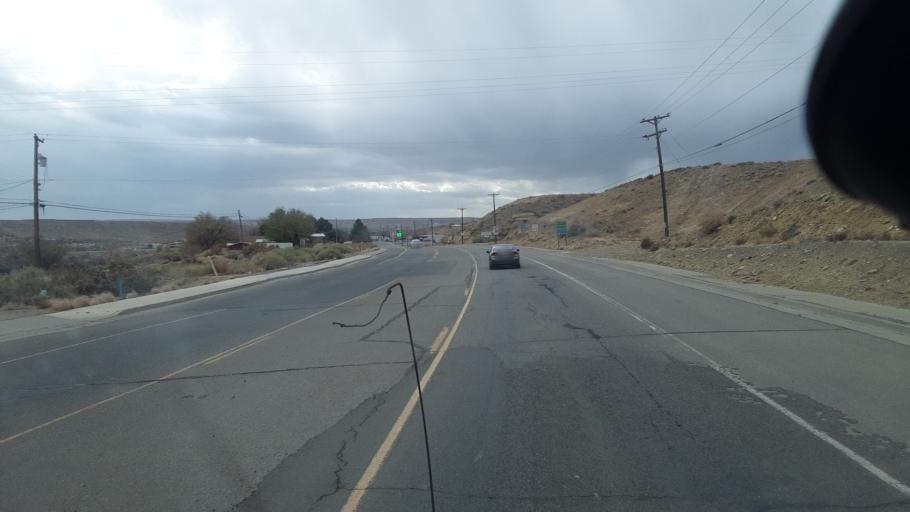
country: US
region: New Mexico
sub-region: San Juan County
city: Farmington
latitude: 36.7633
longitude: -108.2402
